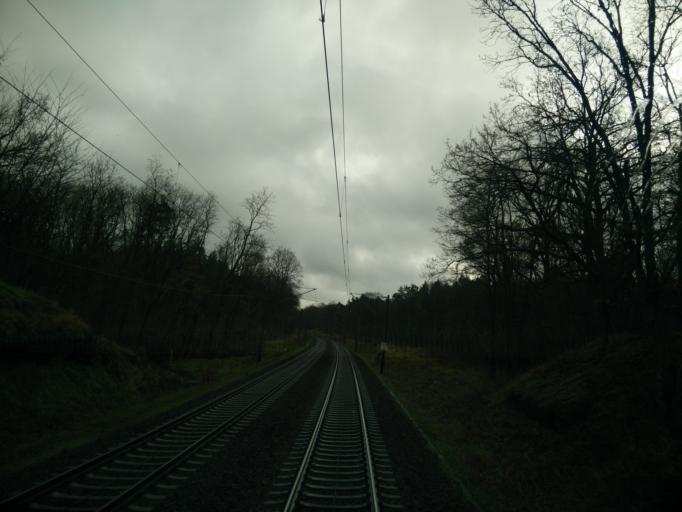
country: DE
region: Mecklenburg-Vorpommern
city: Ludwigslust
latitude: 53.3149
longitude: 11.5116
